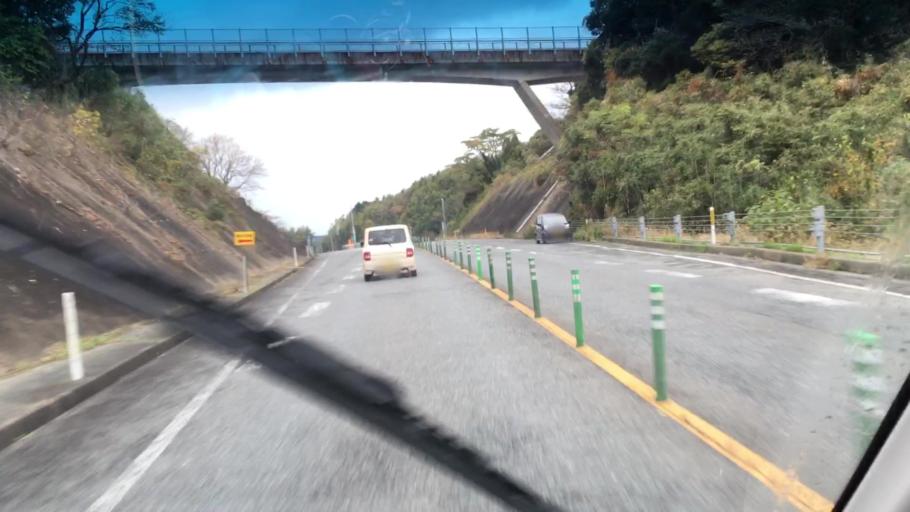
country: JP
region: Fukuoka
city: Maebaru-chuo
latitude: 33.5040
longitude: 130.1003
